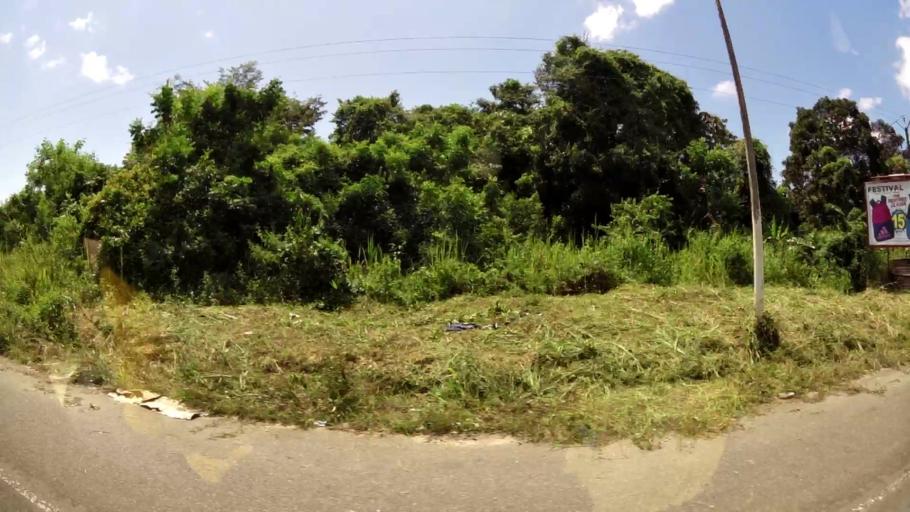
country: GF
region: Guyane
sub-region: Guyane
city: Matoury
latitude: 4.8822
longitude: -52.3362
